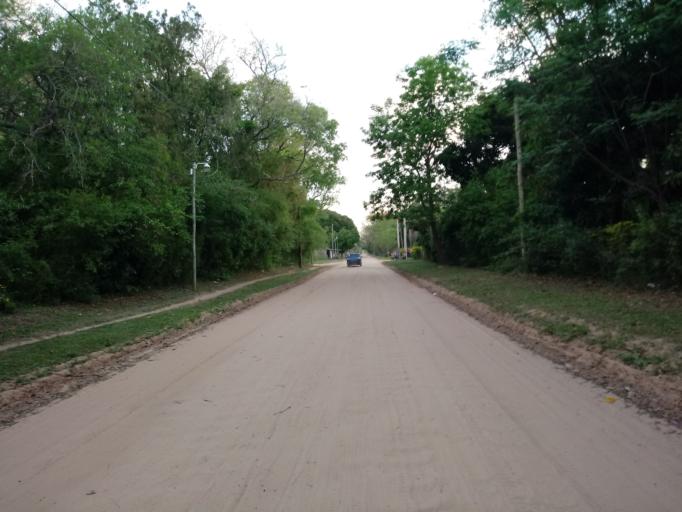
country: AR
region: Corrientes
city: San Luis del Palmar
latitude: -27.4517
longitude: -58.6547
